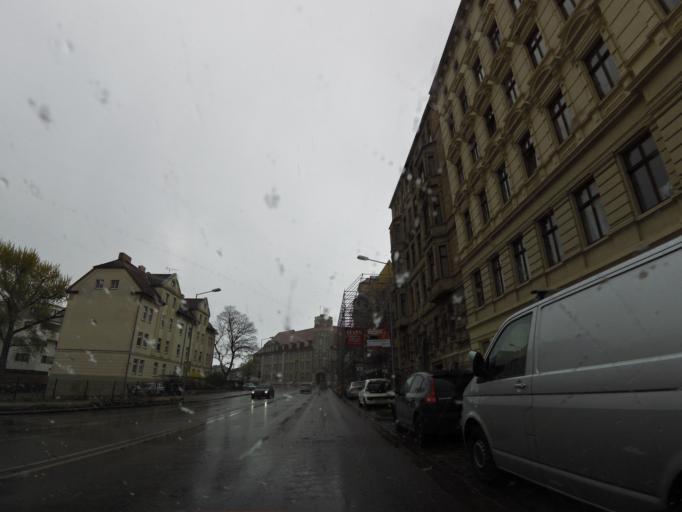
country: DE
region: Saxony-Anhalt
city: Magdeburg
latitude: 52.1189
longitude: 11.6312
